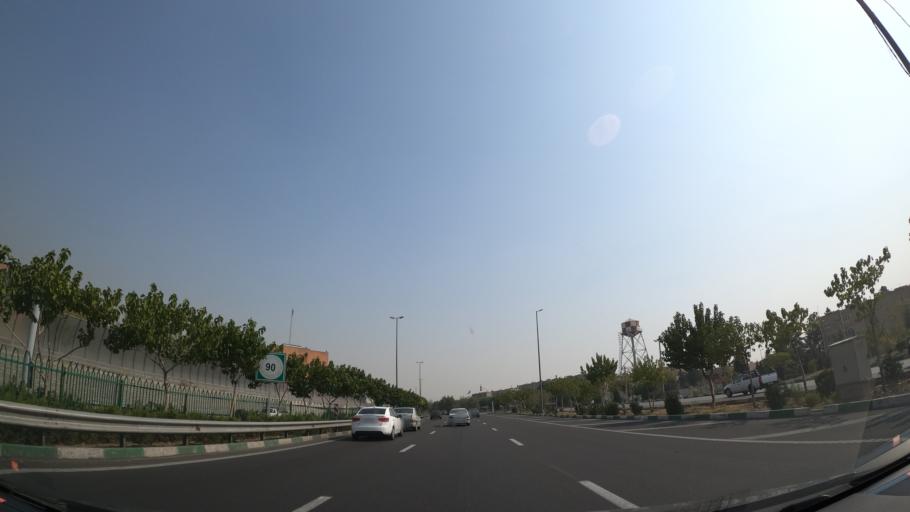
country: IR
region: Tehran
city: Shahr-e Qods
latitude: 35.7582
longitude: 51.2599
